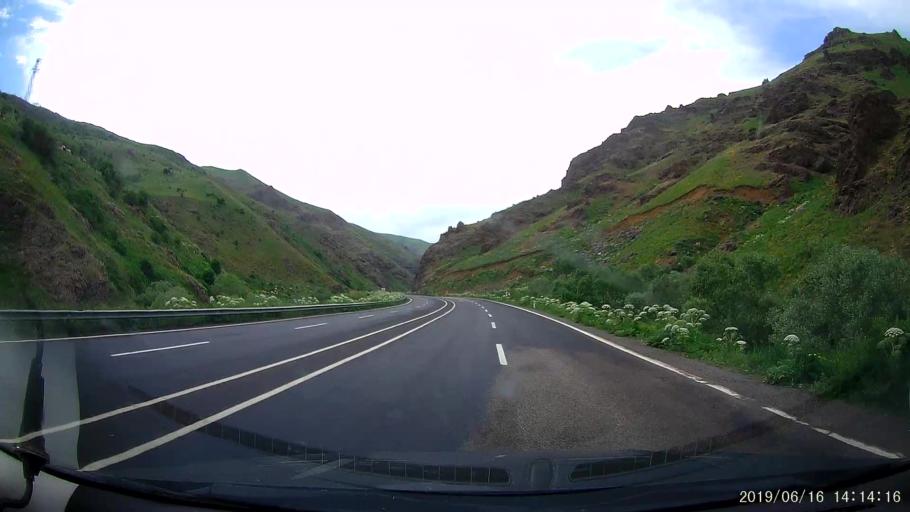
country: TR
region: Agri
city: Tahir
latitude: 39.7950
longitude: 42.5012
